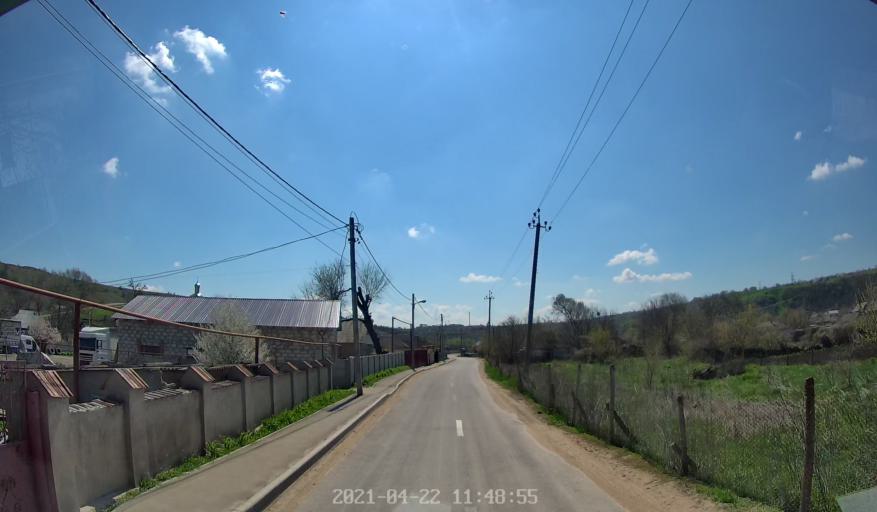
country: MD
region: Chisinau
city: Ciorescu
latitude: 47.1454
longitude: 28.8964
